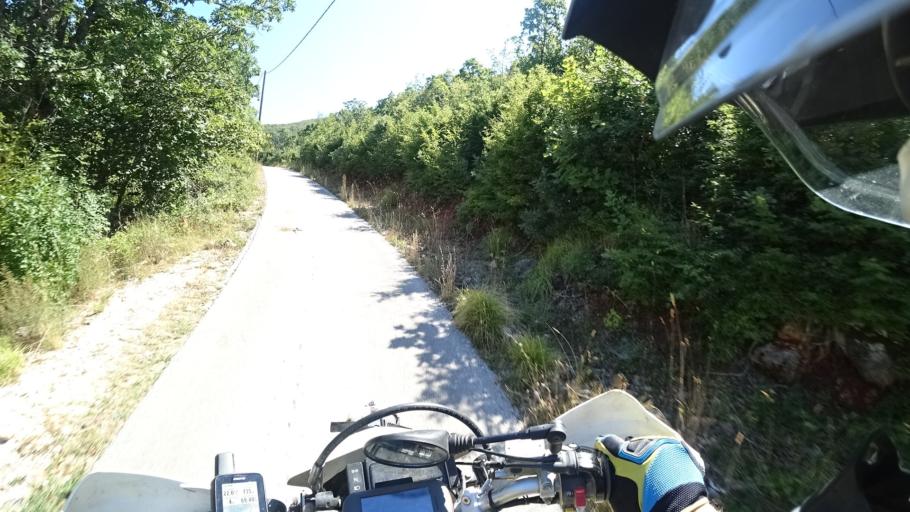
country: HR
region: Sibensko-Kniniska
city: Drnis
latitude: 43.8131
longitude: 16.3852
